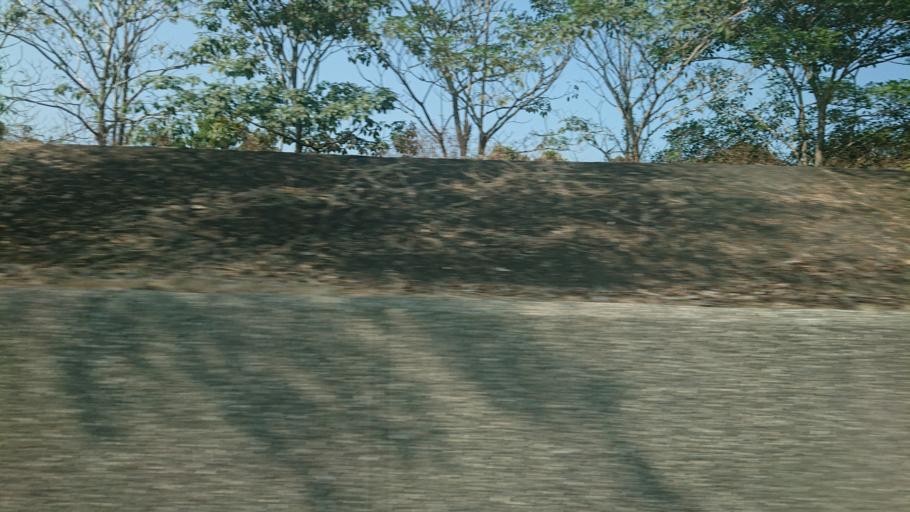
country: TW
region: Taiwan
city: Lugu
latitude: 23.7510
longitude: 120.6588
